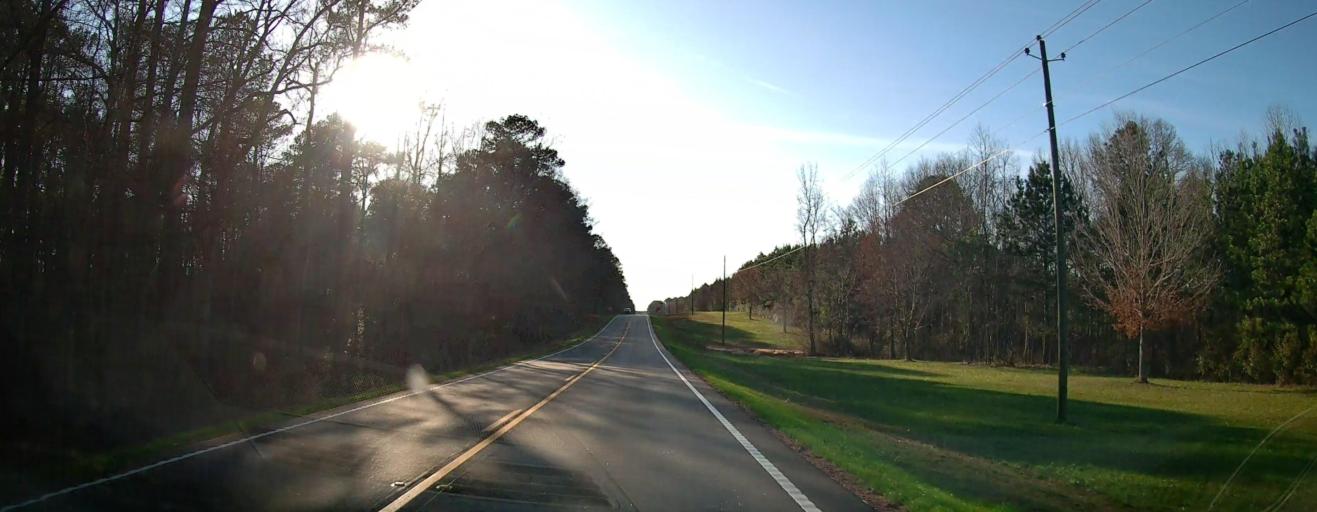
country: US
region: Georgia
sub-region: Harris County
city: Hamilton
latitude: 32.7473
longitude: -85.0045
